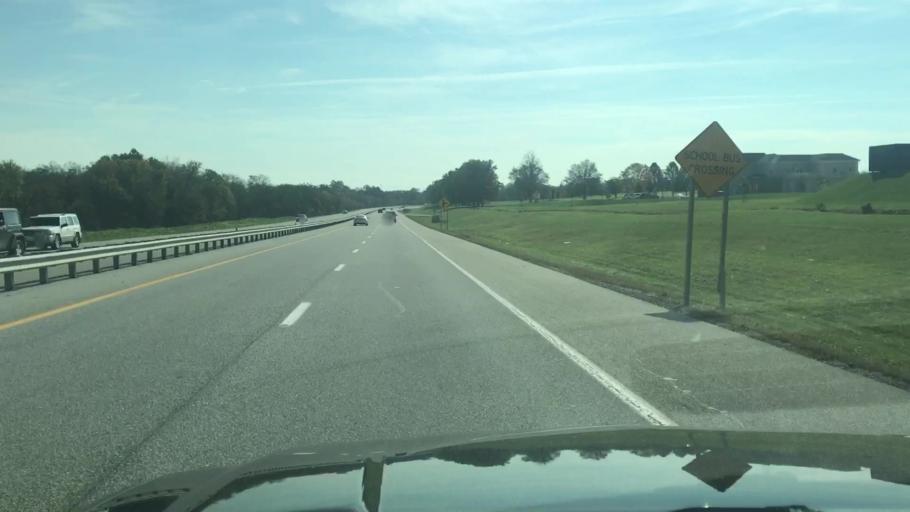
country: US
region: Pennsylvania
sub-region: Cumberland County
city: Mechanicsburg
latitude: 40.2608
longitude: -77.0386
